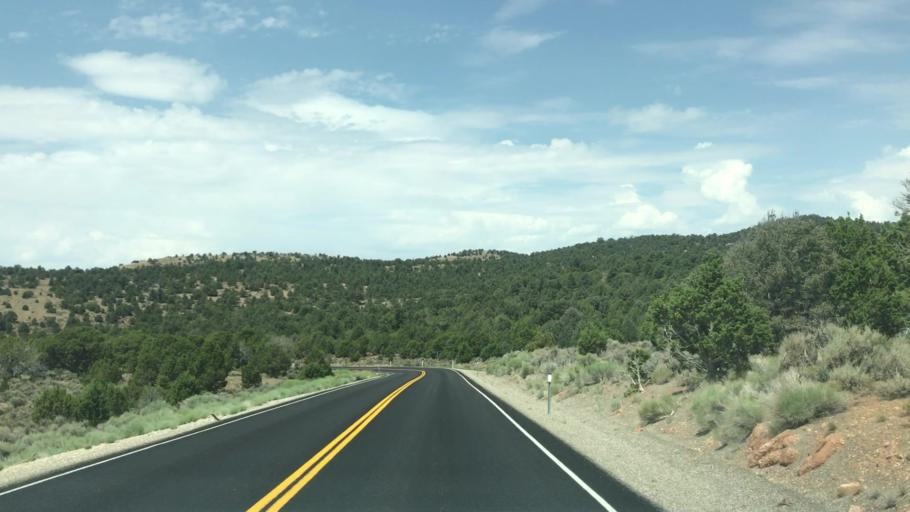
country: US
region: Nevada
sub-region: Eureka County
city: Eureka
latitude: 39.3981
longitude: -115.4711
